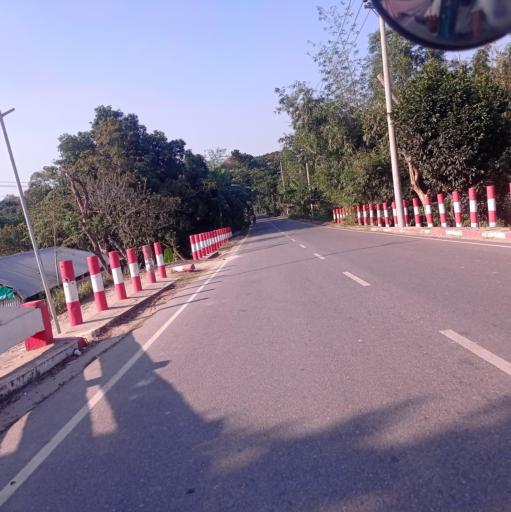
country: BD
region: Dhaka
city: Bajitpur
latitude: 24.1435
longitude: 90.8162
